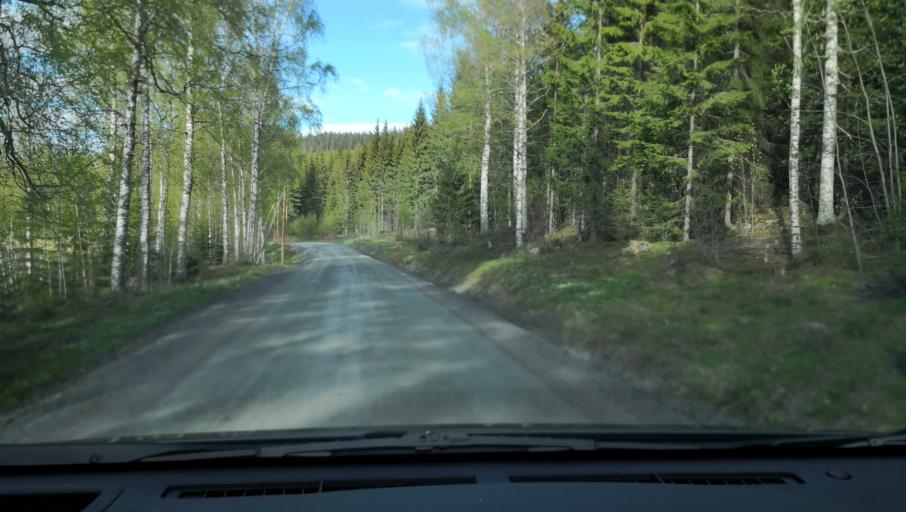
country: SE
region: Dalarna
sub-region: Saters Kommun
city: Saeter
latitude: 60.2726
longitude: 15.8340
